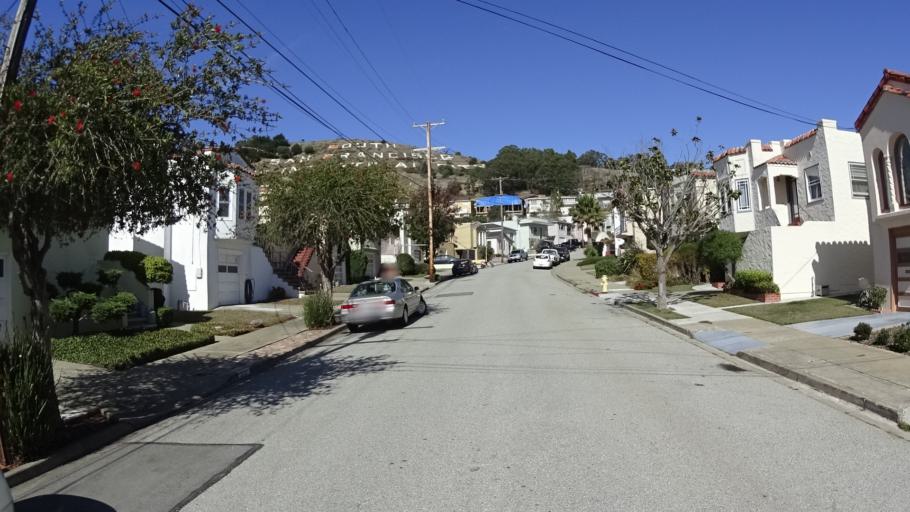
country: US
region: California
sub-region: San Mateo County
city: South San Francisco
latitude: 37.6597
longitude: -122.4181
